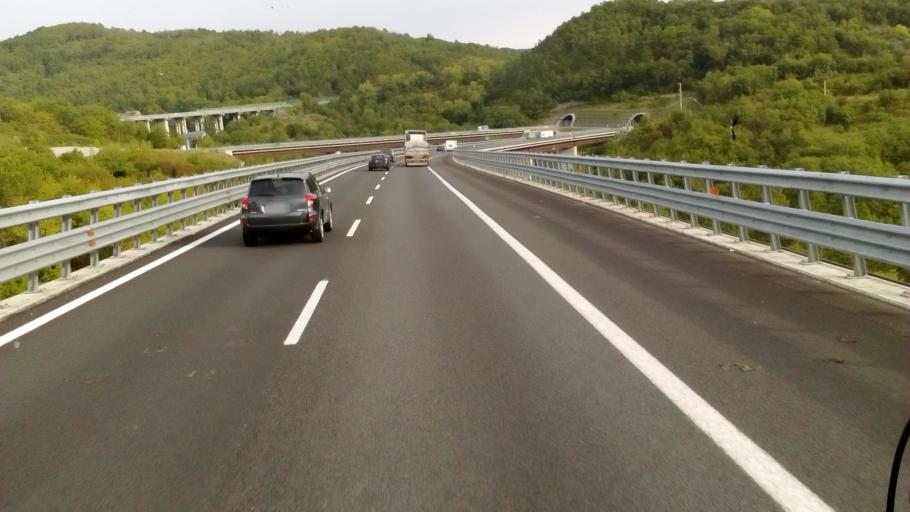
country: IT
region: Tuscany
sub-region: Province of Florence
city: Barberino di Mugello
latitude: 44.0335
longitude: 11.2264
